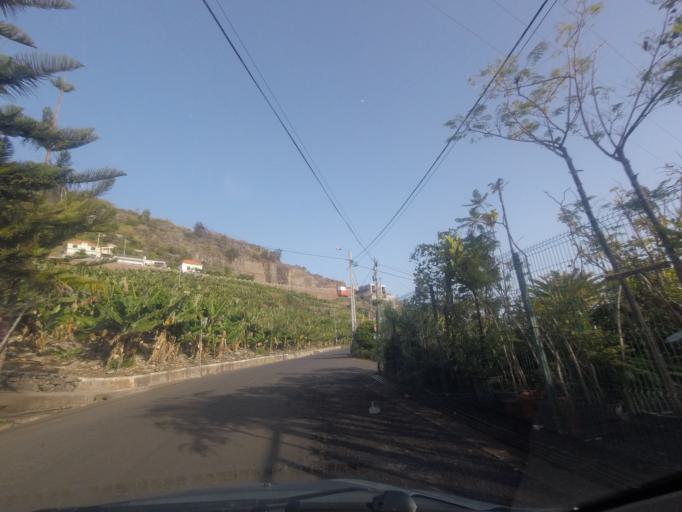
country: PT
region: Madeira
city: Ponta do Sol
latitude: 32.6817
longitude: -17.0733
